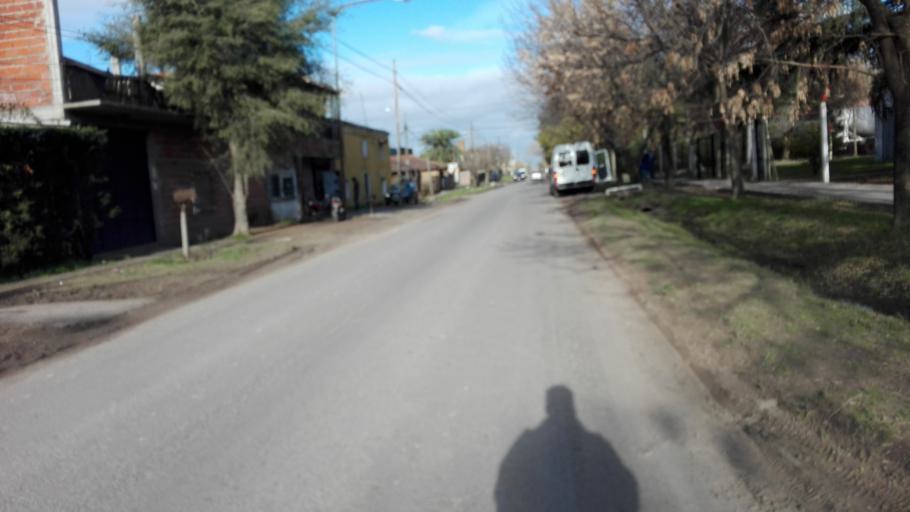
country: AR
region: Buenos Aires
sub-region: Partido de La Plata
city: La Plata
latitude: -34.9163
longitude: -58.0219
